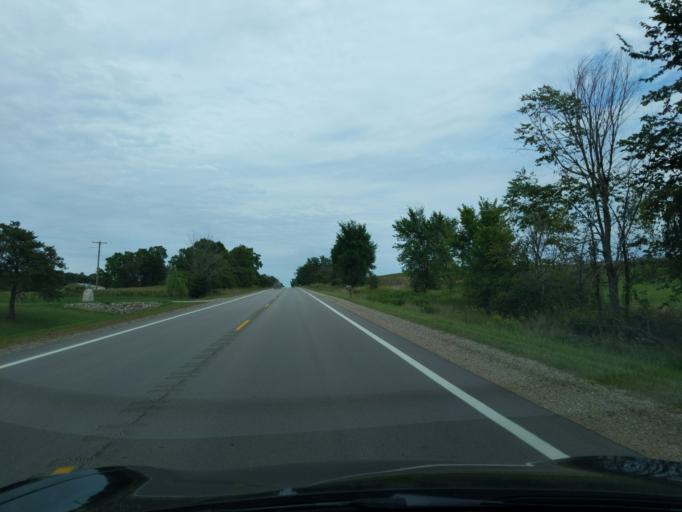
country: US
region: Michigan
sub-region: Barry County
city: Nashville
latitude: 42.5672
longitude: -85.0452
